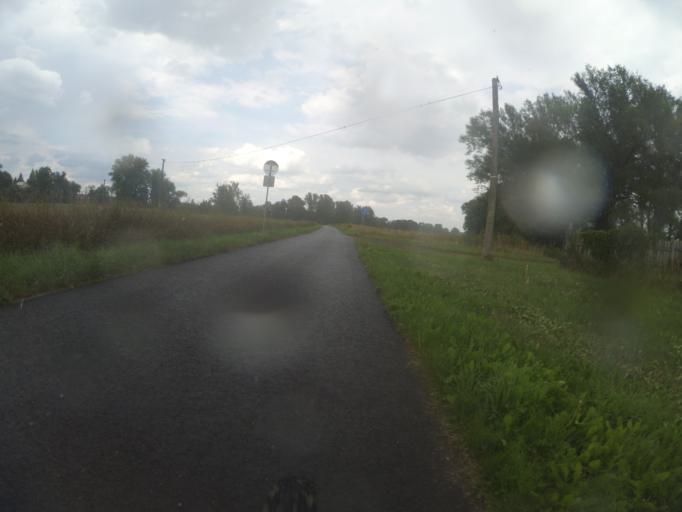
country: CZ
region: Central Bohemia
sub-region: Okres Melnik
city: Melnik
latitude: 50.3206
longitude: 14.4506
